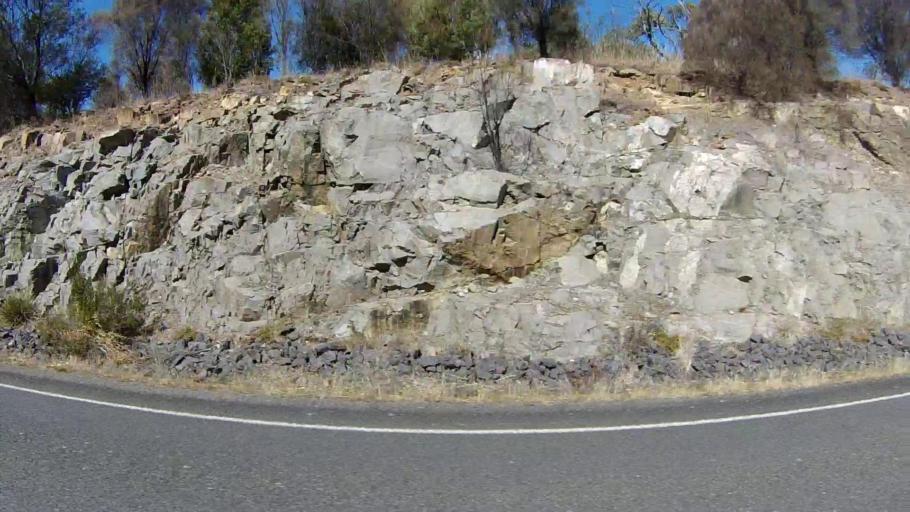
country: AU
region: Tasmania
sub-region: Sorell
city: Sorell
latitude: -42.5866
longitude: 147.8005
